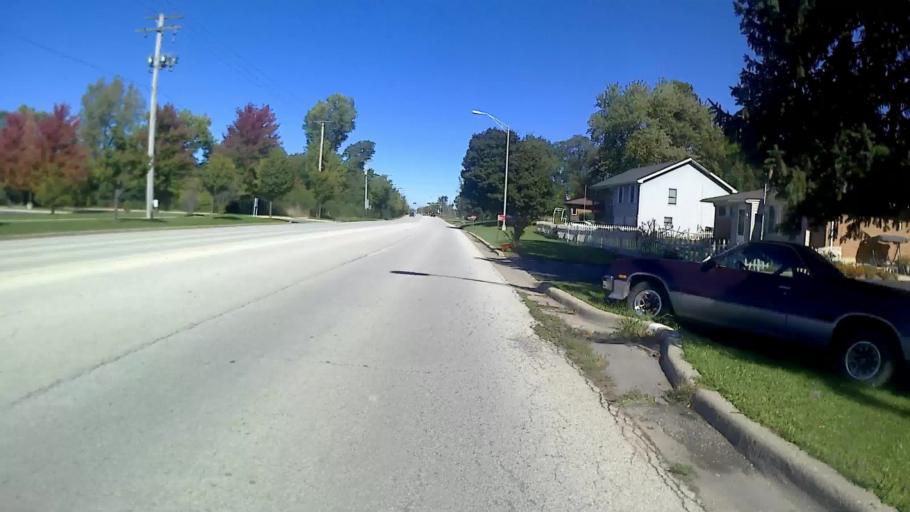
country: US
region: Illinois
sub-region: DuPage County
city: Villa Park
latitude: 41.9076
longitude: -88.0078
